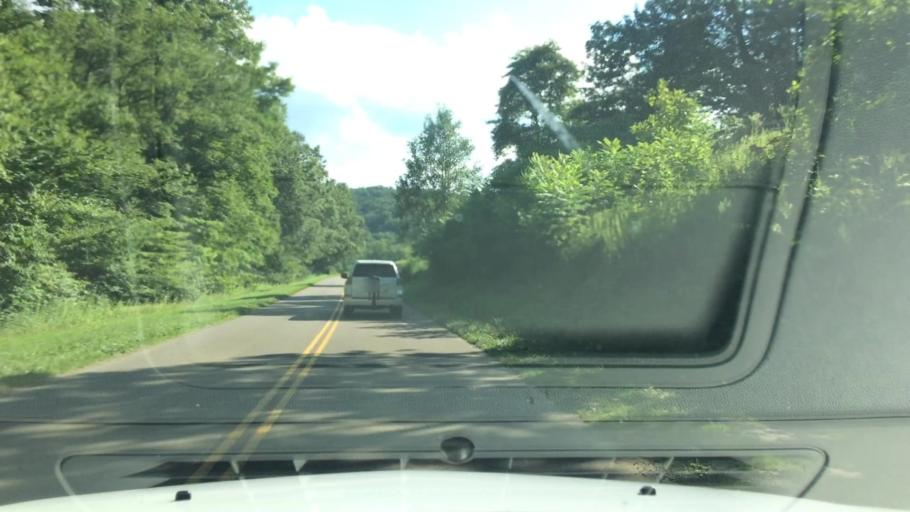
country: US
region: North Carolina
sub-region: Watauga County
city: Blowing Rock
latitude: 36.1408
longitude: -81.7218
